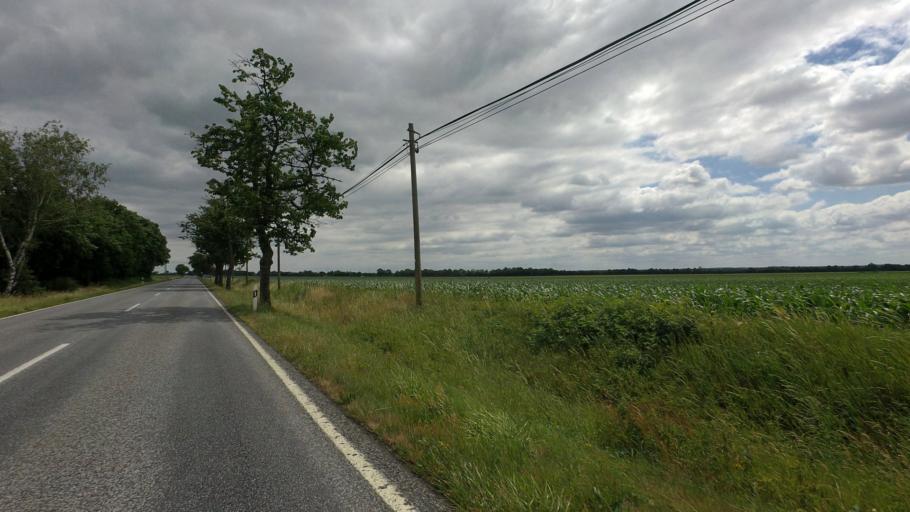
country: DE
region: Brandenburg
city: Luckau
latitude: 51.8296
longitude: 13.7779
